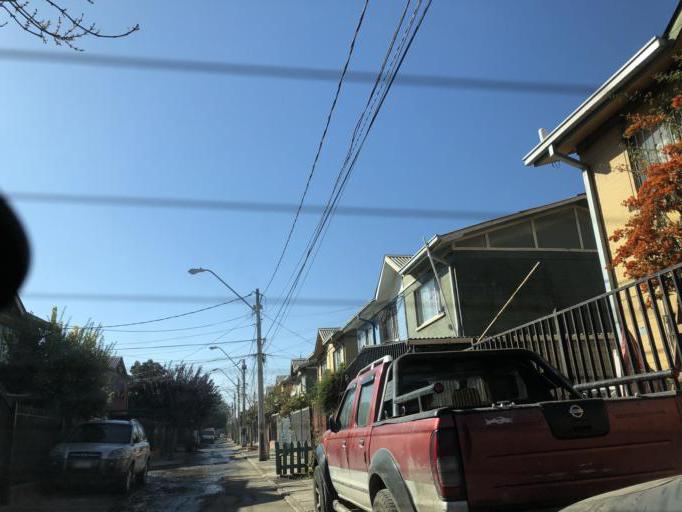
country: CL
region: Santiago Metropolitan
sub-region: Provincia de Santiago
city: La Pintana
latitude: -33.6308
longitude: -70.6217
